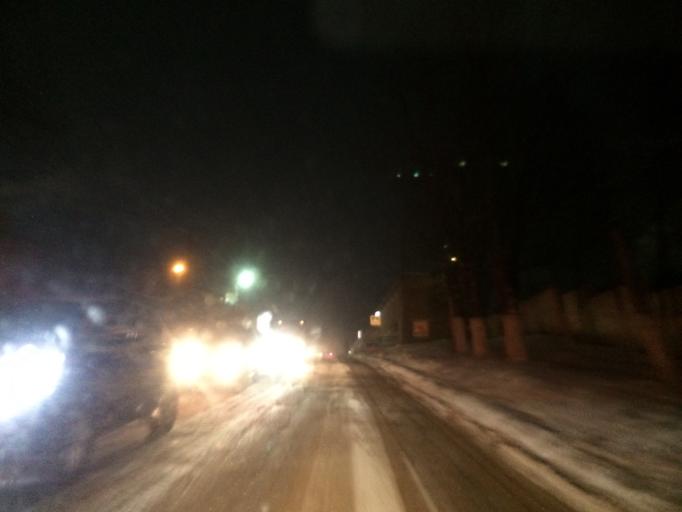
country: RU
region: Tula
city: Mendeleyevskiy
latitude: 54.1582
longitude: 37.6054
